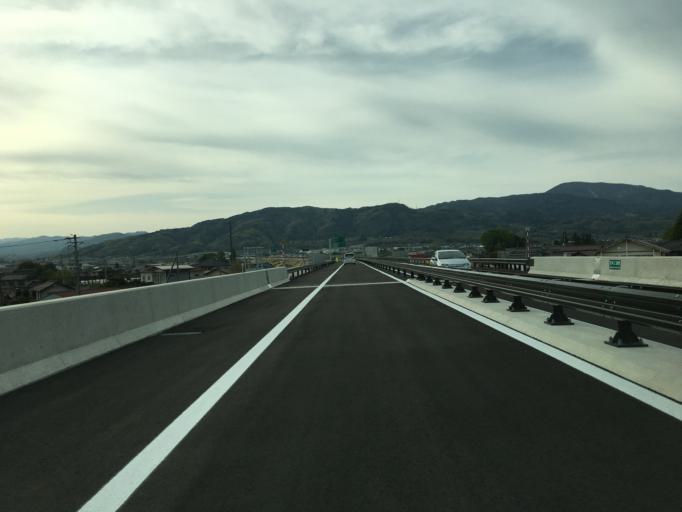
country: JP
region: Fukushima
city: Hobaramachi
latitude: 37.8216
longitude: 140.5238
